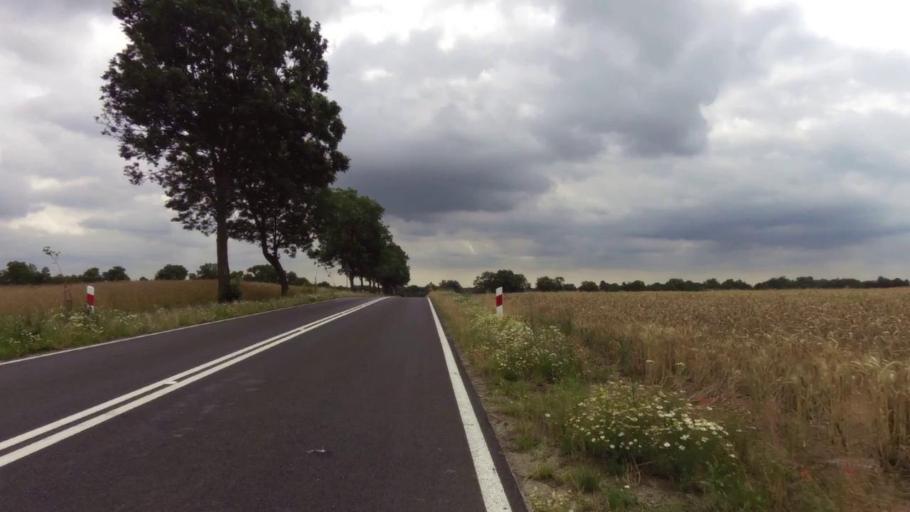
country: PL
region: West Pomeranian Voivodeship
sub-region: Powiat gryfinski
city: Cedynia
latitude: 52.8670
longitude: 14.2556
